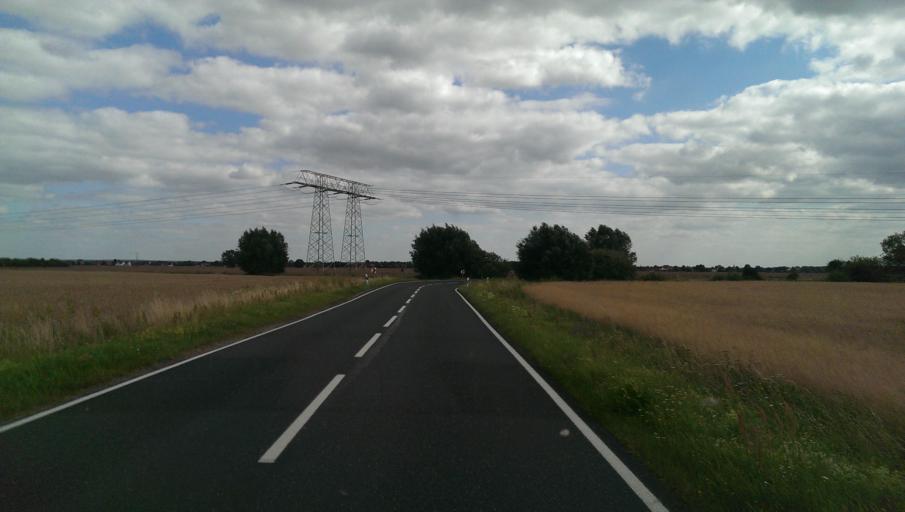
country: DE
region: Saxony-Anhalt
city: Worlitz
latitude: 51.8296
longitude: 12.4162
